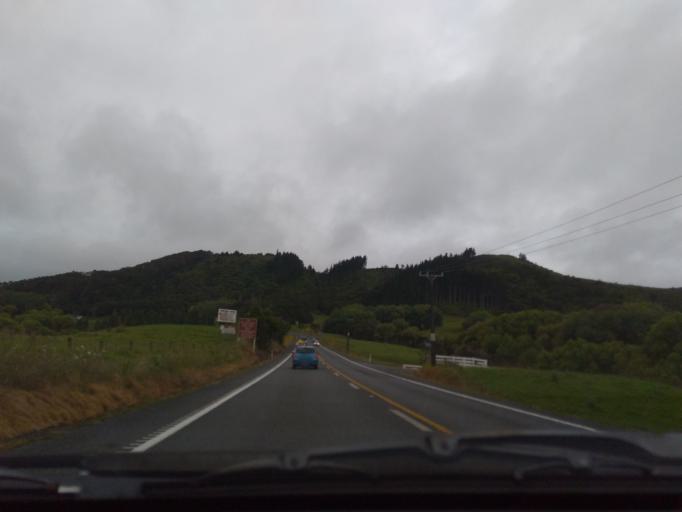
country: NZ
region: Northland
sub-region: Whangarei
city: Ruakaka
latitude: -36.1021
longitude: 174.4332
